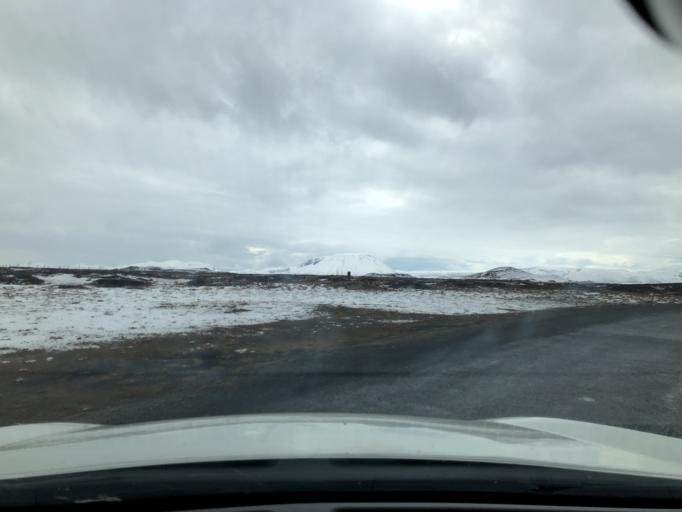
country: IS
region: Northeast
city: Laugar
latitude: 65.6445
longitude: -16.8043
